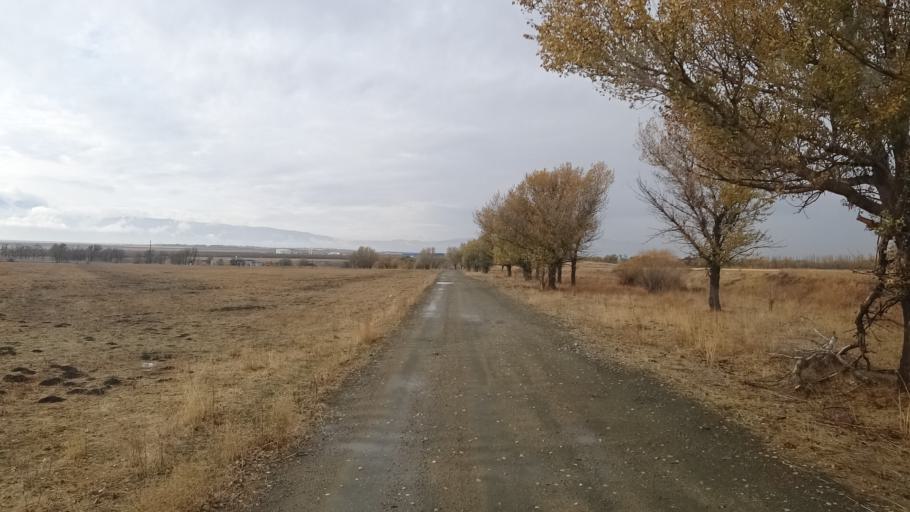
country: KZ
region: Ongtustik Qazaqstan
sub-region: Tulkibas Audany
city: Zhabagly
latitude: 42.5194
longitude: 70.5114
